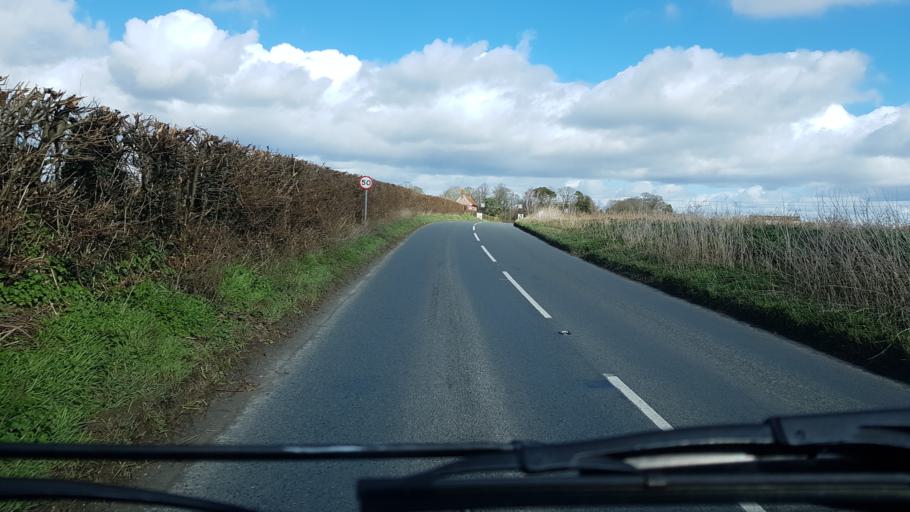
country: GB
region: England
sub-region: Wiltshire
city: Market Lavington
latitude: 51.3078
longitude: -1.9545
